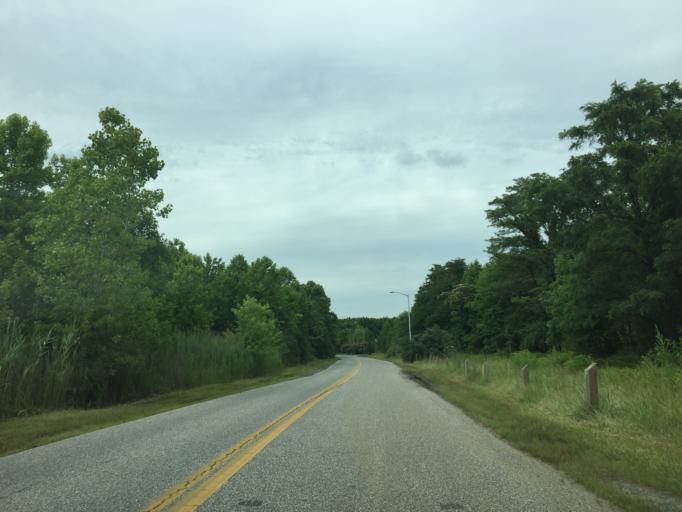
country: US
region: Maryland
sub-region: Baltimore County
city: Edgemere
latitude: 39.2622
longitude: -76.4561
